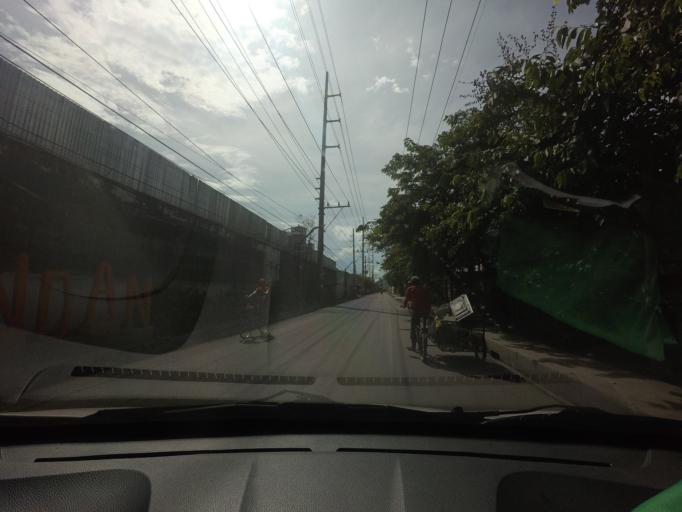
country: PH
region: Calabarzon
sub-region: Province of Rizal
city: Pateros
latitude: 14.5404
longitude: 121.0900
